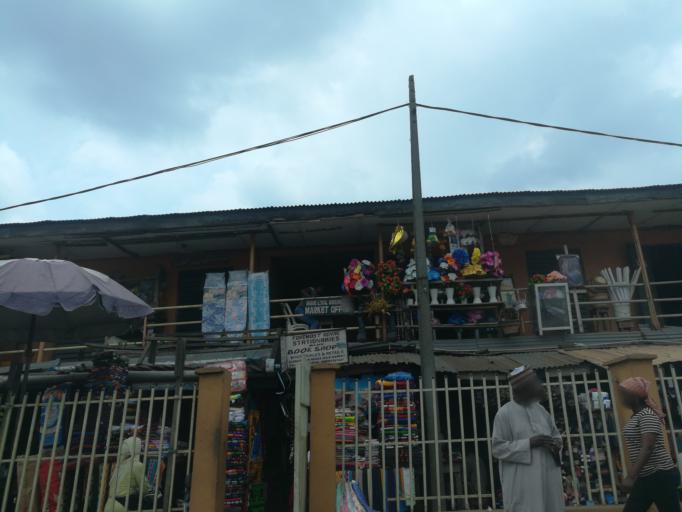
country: NG
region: Lagos
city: Agege
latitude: 6.6203
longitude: 3.3255
